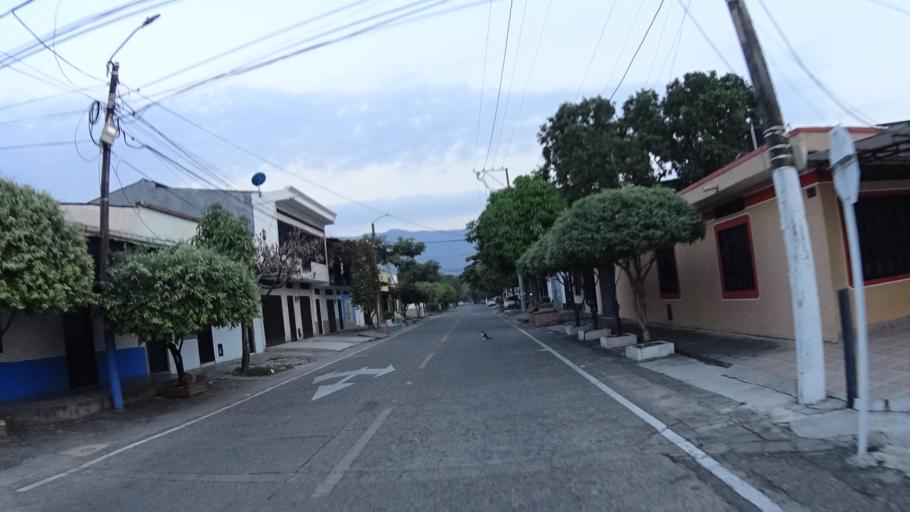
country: CO
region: Caldas
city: La Dorada
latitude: 5.4455
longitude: -74.6609
